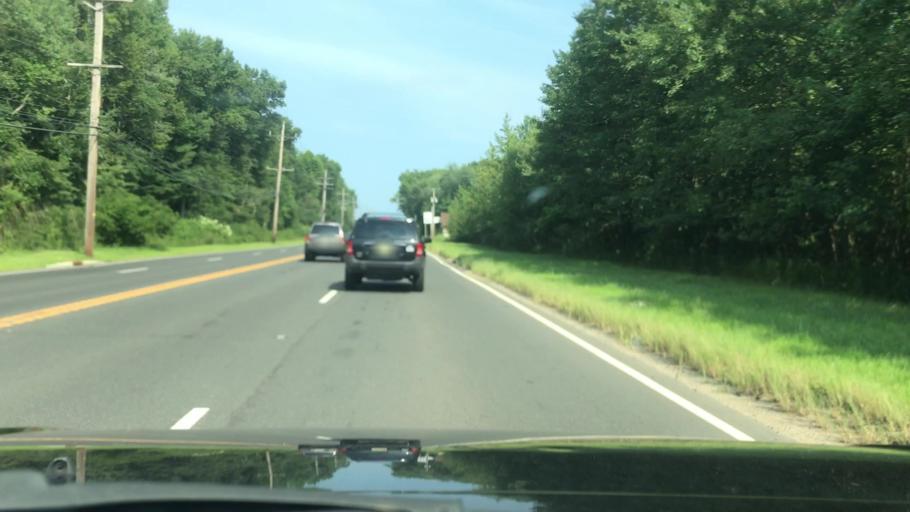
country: US
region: New Jersey
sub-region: Monmouth County
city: Farmingdale
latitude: 40.2182
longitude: -74.1127
